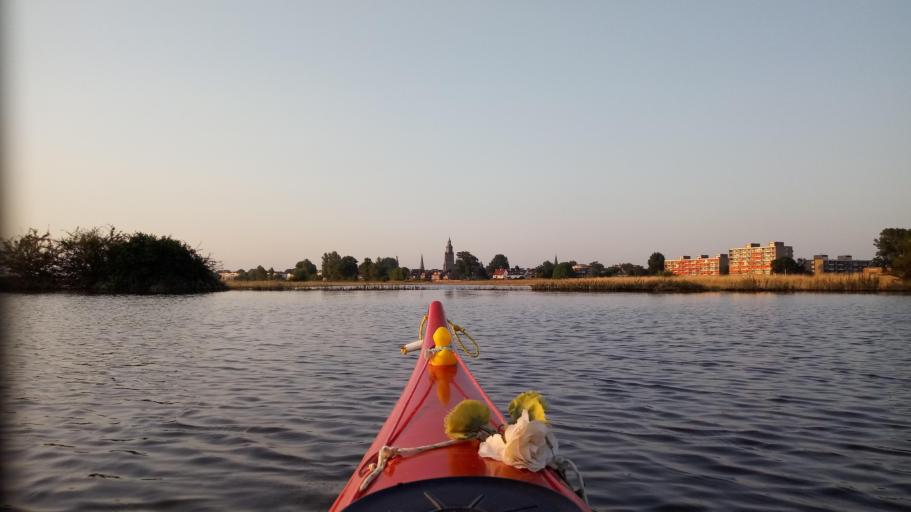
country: NL
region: Gelderland
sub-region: Gemeente Zutphen
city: Zutphen
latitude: 52.1304
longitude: 6.1873
